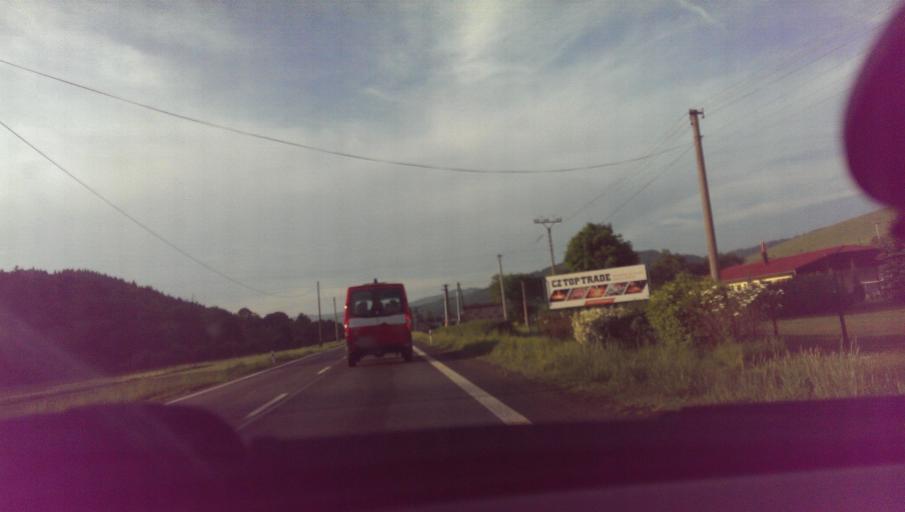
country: CZ
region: Zlin
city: Valasska Polanka
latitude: 49.3004
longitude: 18.0018
